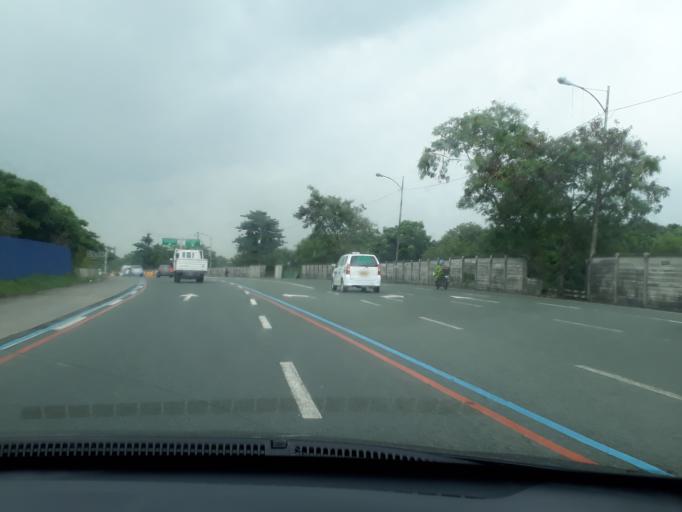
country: PH
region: Metro Manila
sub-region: Makati City
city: Makati City
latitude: 14.5162
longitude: 121.0382
